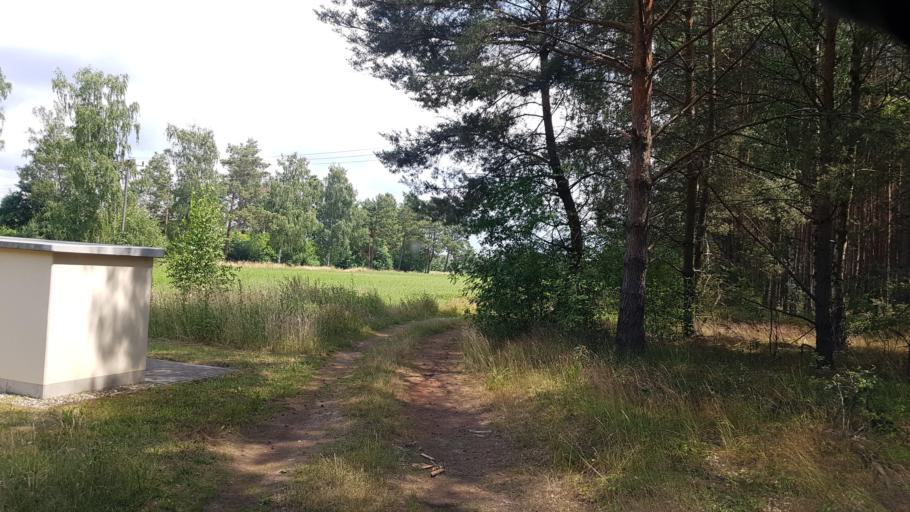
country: DE
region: Brandenburg
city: Crinitz
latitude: 51.7548
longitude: 13.8474
